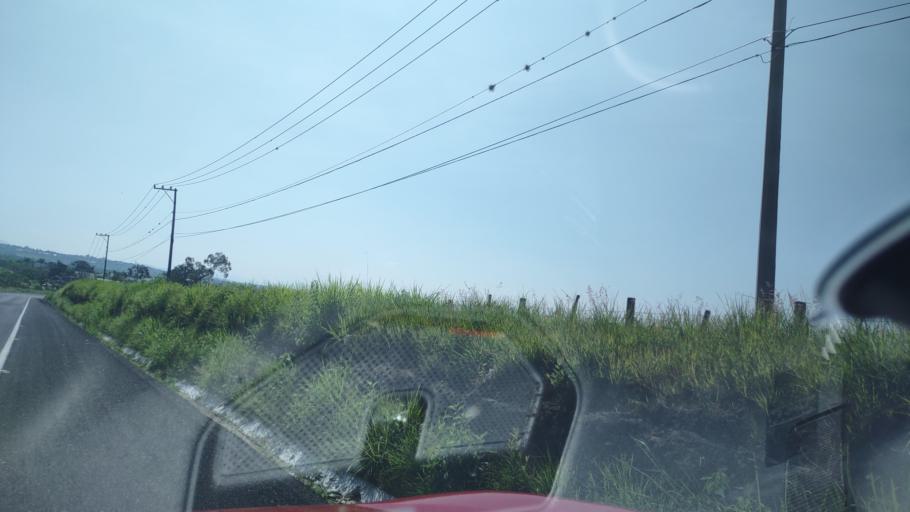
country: MX
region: Veracruz
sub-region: Emiliano Zapata
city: Jacarandas
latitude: 19.5002
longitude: -96.8311
